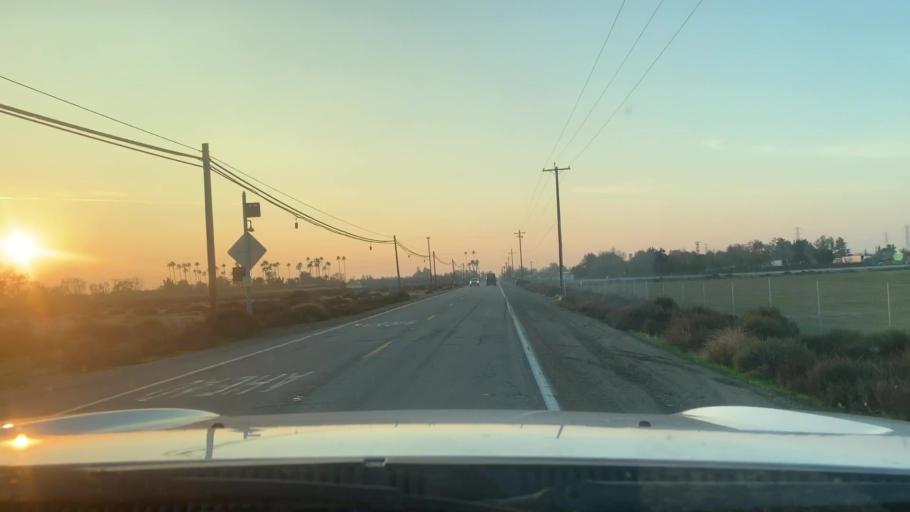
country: US
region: California
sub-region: Kern County
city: Rosedale
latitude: 35.3835
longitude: -119.1837
